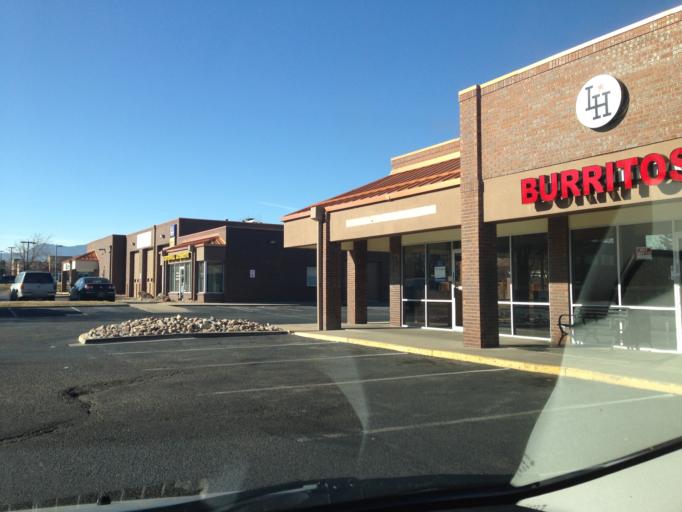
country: US
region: Colorado
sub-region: Boulder County
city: Superior
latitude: 39.9656
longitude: -105.1620
